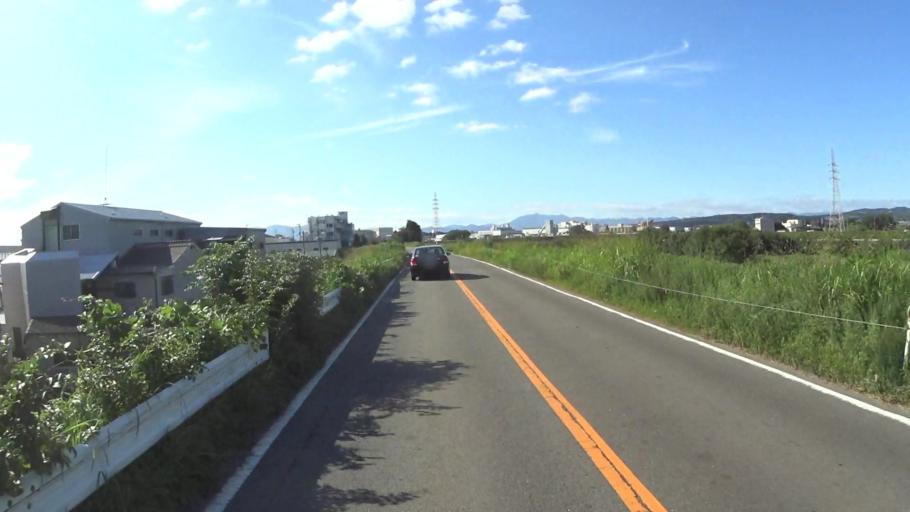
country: JP
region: Kyoto
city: Uji
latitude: 34.9021
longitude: 135.7930
